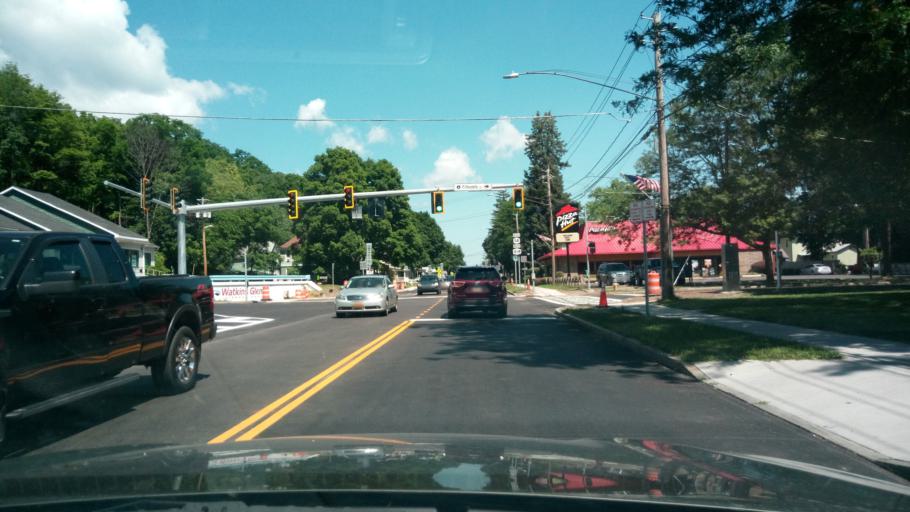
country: US
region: New York
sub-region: Schuyler County
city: Watkins Glen
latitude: 42.3716
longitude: -76.8686
